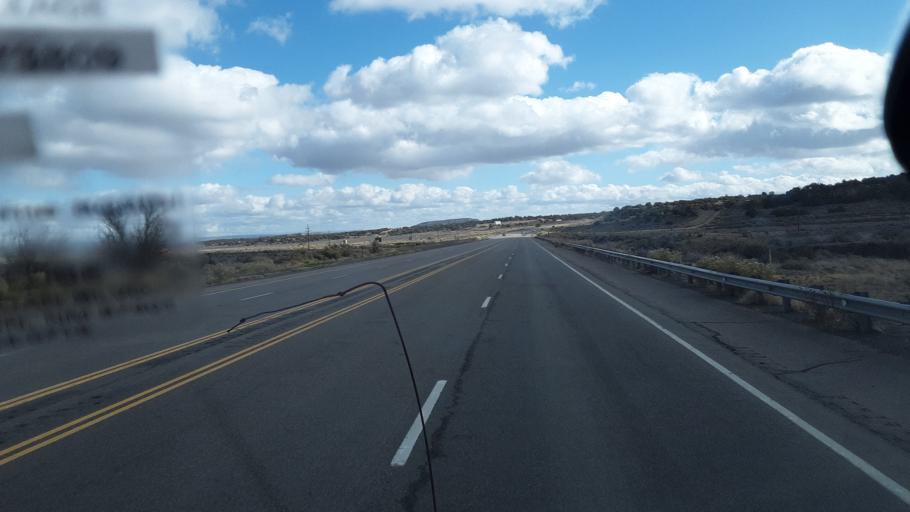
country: US
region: New Mexico
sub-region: San Juan County
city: Bloomfield
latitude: 36.2270
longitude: -107.5153
